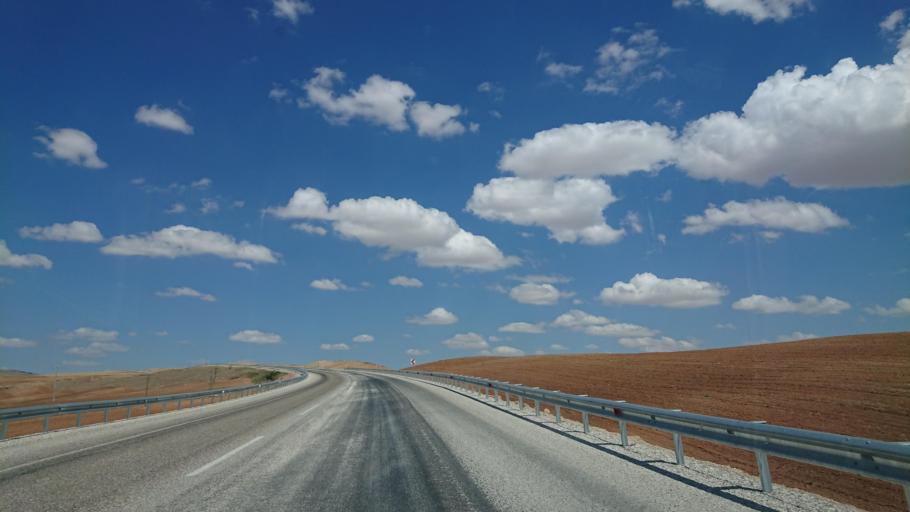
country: TR
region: Ankara
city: Evren
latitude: 39.1069
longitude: 33.9197
